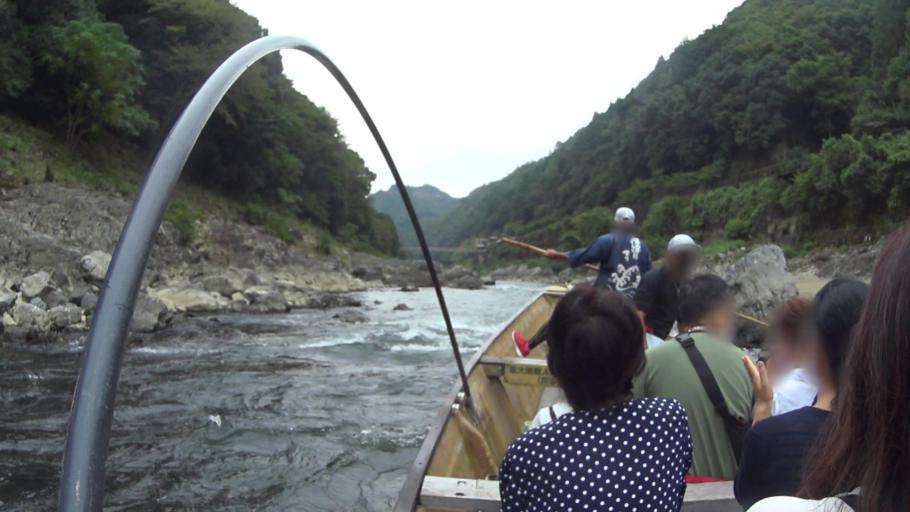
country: JP
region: Kyoto
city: Kameoka
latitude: 35.0245
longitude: 135.6434
